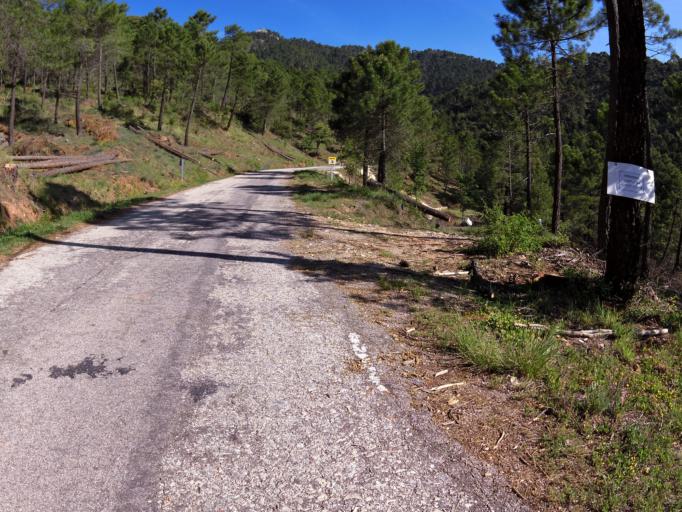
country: ES
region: Castille-La Mancha
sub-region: Provincia de Albacete
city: Riopar
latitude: 38.5208
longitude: -2.4554
